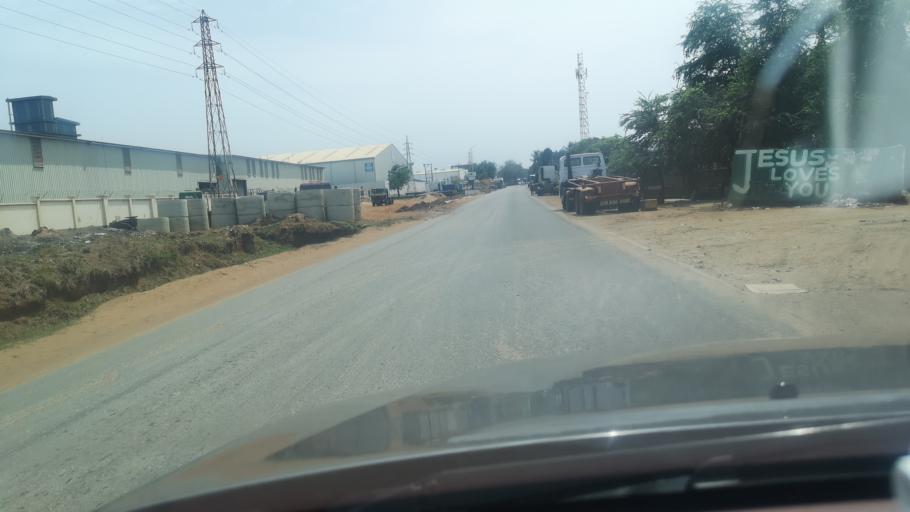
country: GH
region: Greater Accra
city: Tema
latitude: 5.6255
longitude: -0.0158
